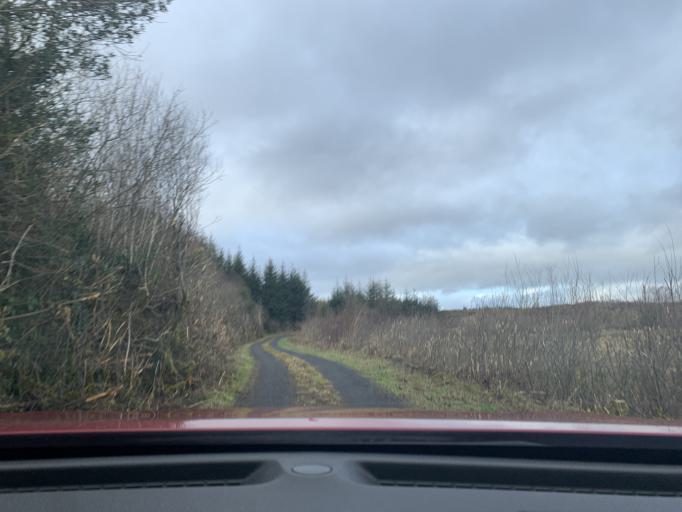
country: IE
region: Connaught
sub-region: Roscommon
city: Ballaghaderreen
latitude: 53.9274
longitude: -8.5597
